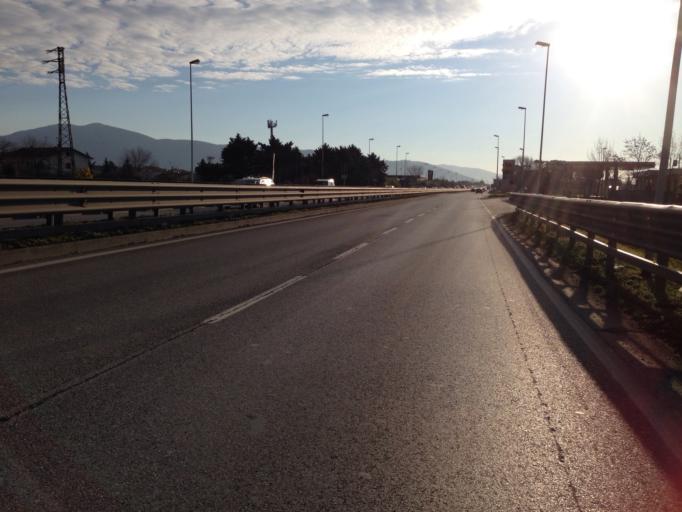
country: IT
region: Tuscany
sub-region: Provincia di Prato
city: Fornacelle
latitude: 43.8834
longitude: 11.0423
